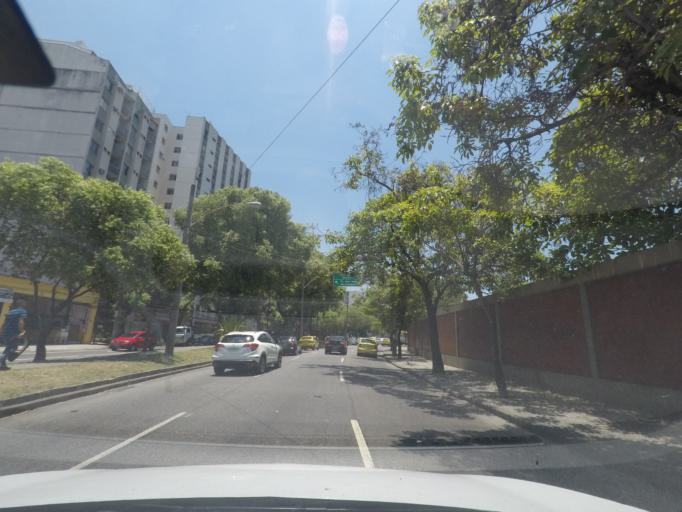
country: BR
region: Rio de Janeiro
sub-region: Rio De Janeiro
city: Rio de Janeiro
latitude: -22.9106
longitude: -43.2379
